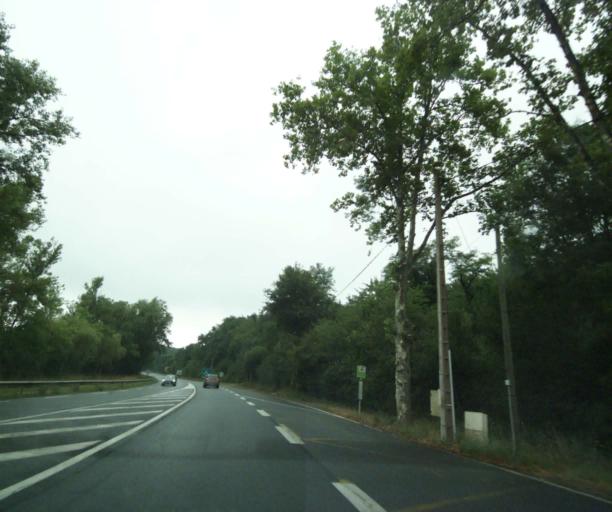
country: FR
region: Midi-Pyrenees
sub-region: Departement du Tarn
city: Le Garric
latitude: 43.9920
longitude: 2.1744
